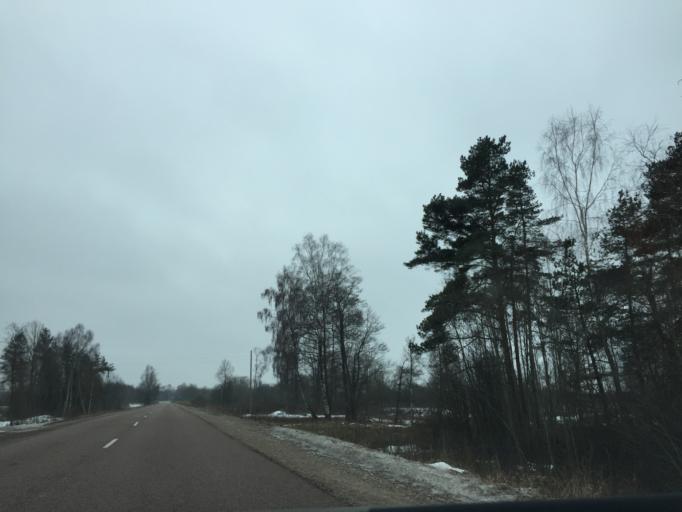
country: LV
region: Olaine
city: Olaine
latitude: 56.6324
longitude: 23.9344
